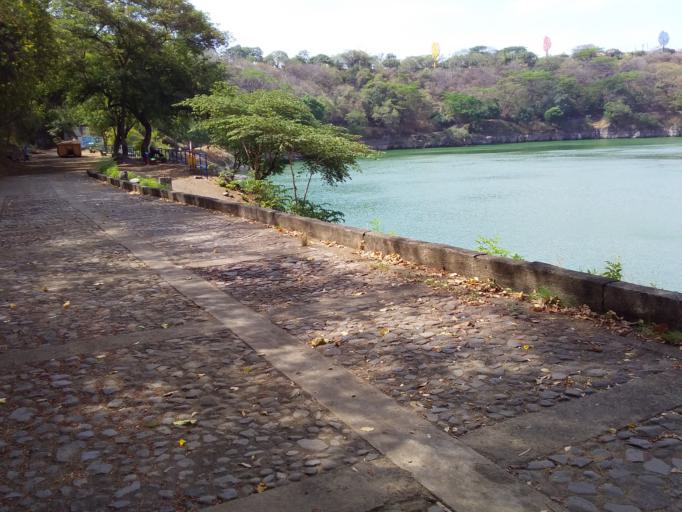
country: NI
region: Managua
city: Managua
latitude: 12.1406
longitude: -86.2686
